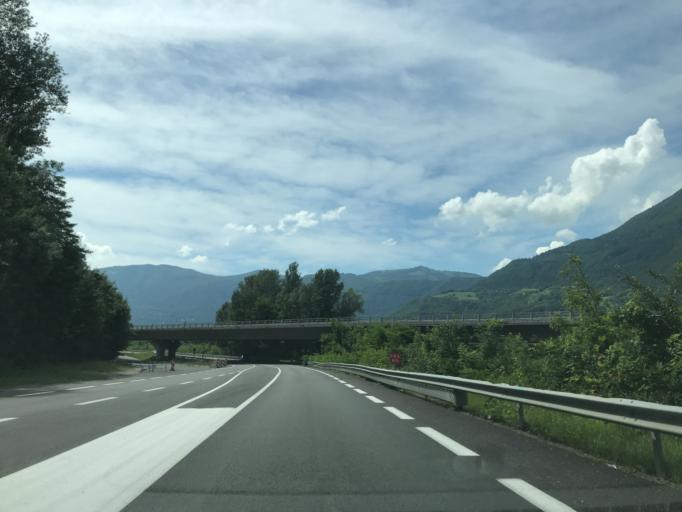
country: FR
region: Rhone-Alpes
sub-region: Departement de la Savoie
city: Aiton
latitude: 45.5622
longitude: 6.2059
